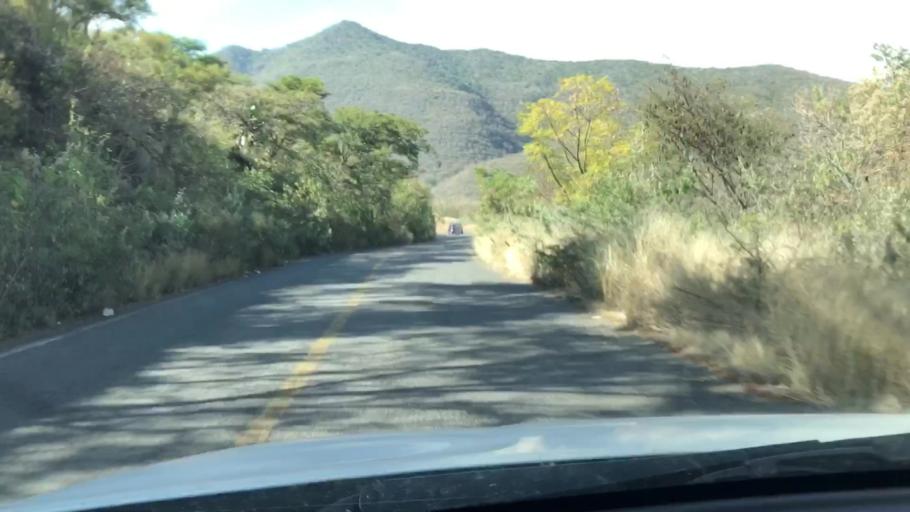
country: MX
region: Jalisco
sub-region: Zacoalco de Torres
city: Barranca de Otates (Barranca de Otatan)
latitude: 20.2563
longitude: -103.6745
